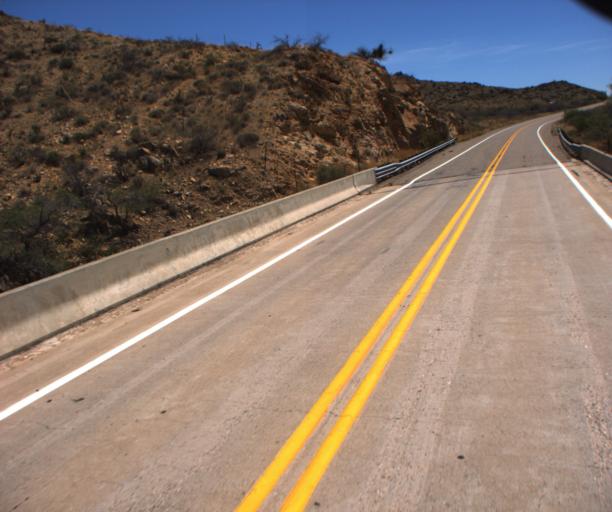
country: US
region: Arizona
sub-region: Mohave County
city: New Kingman-Butler
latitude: 35.3798
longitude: -113.7284
